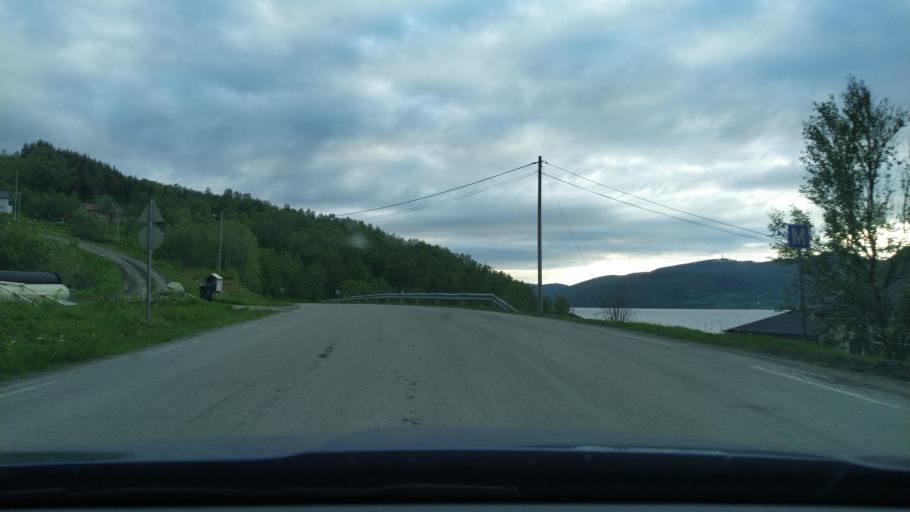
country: NO
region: Troms
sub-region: Lenvik
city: Finnsnes
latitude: 69.1452
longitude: 17.9470
